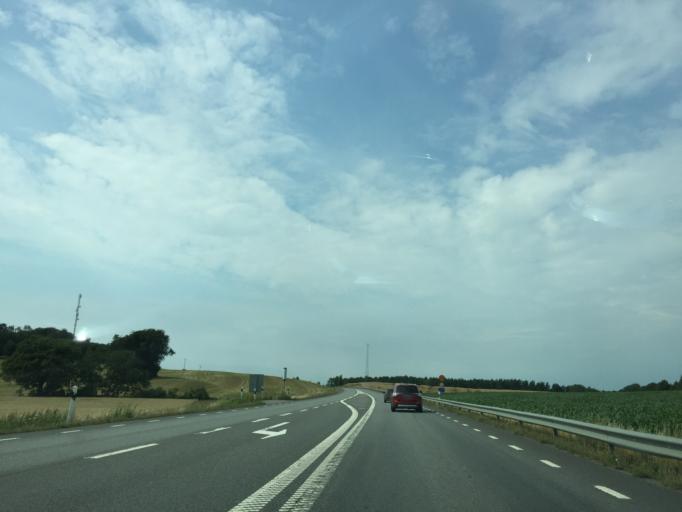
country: SE
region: Skane
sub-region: Tomelilla Kommun
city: Tomelilla
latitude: 55.5859
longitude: 13.8324
